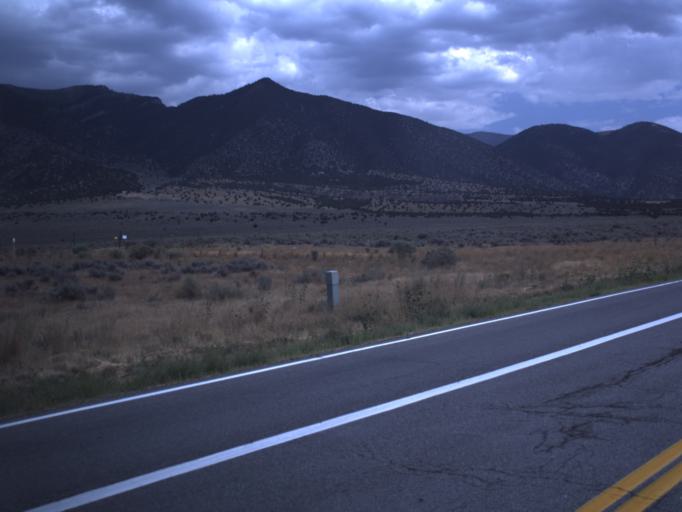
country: US
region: Utah
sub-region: Tooele County
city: Tooele
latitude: 40.3609
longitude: -112.3290
